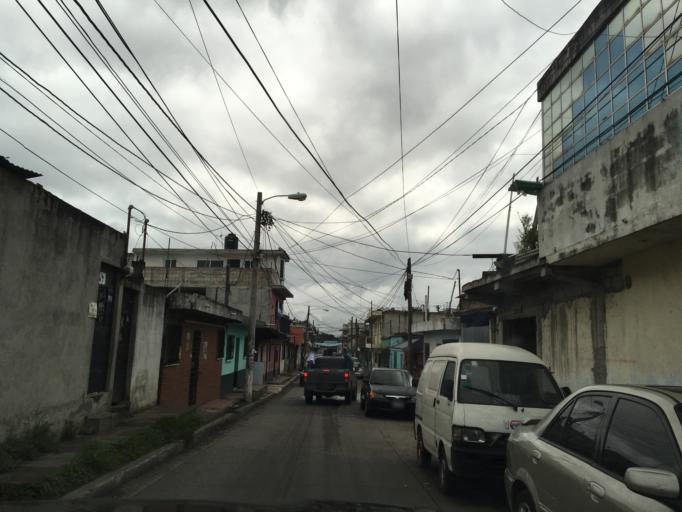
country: GT
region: Guatemala
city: Mixco
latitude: 14.6225
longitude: -90.5860
